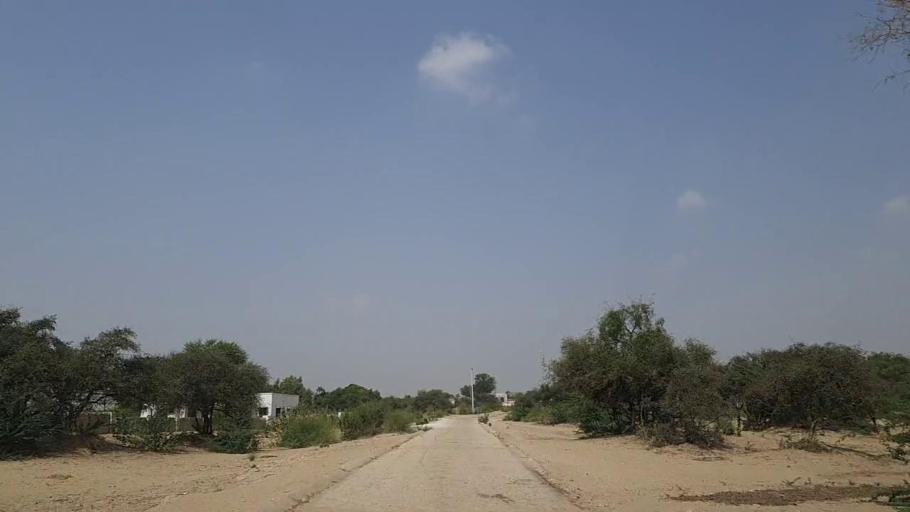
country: PK
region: Sindh
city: Mithi
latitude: 24.7619
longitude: 69.9261
